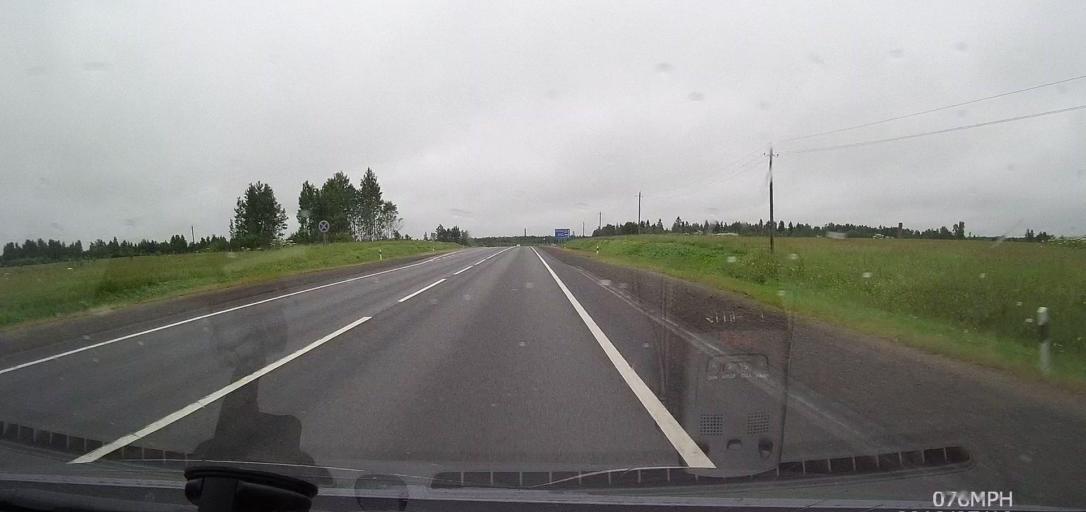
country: RU
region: Leningrad
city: Staraya Ladoga
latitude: 59.9943
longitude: 32.0929
